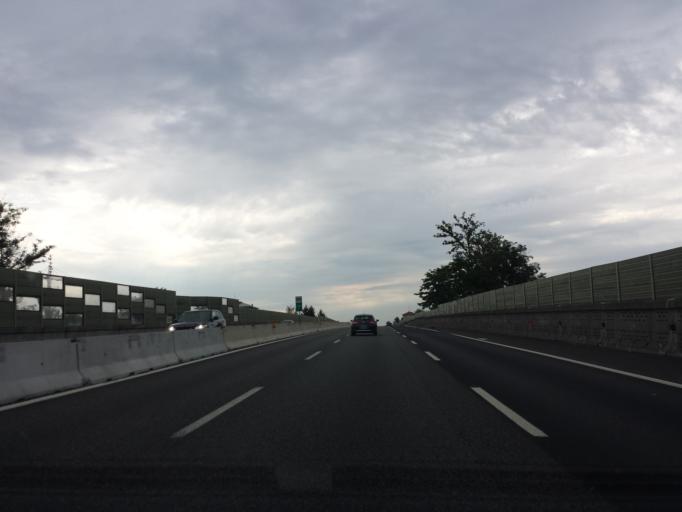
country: IT
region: Lombardy
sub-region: Provincia di Varese
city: Marnate
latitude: 45.6197
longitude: 8.9055
